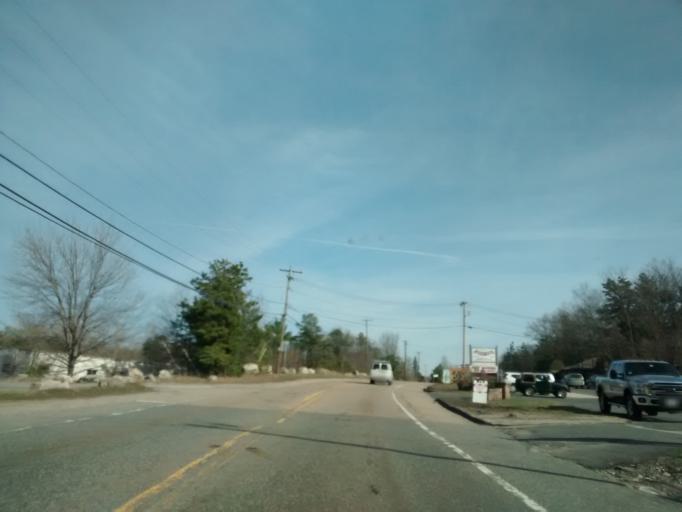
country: US
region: Massachusetts
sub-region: Worcester County
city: Millville
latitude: 42.0286
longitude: -71.6071
